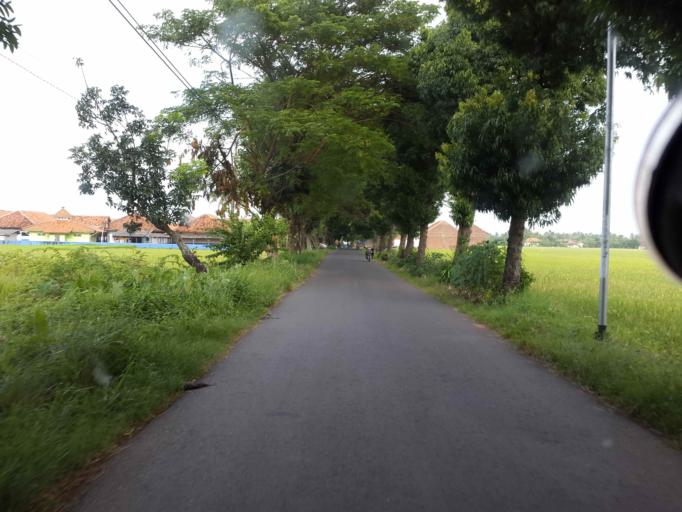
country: ID
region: Central Java
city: Comal
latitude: -6.8376
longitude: 109.5206
